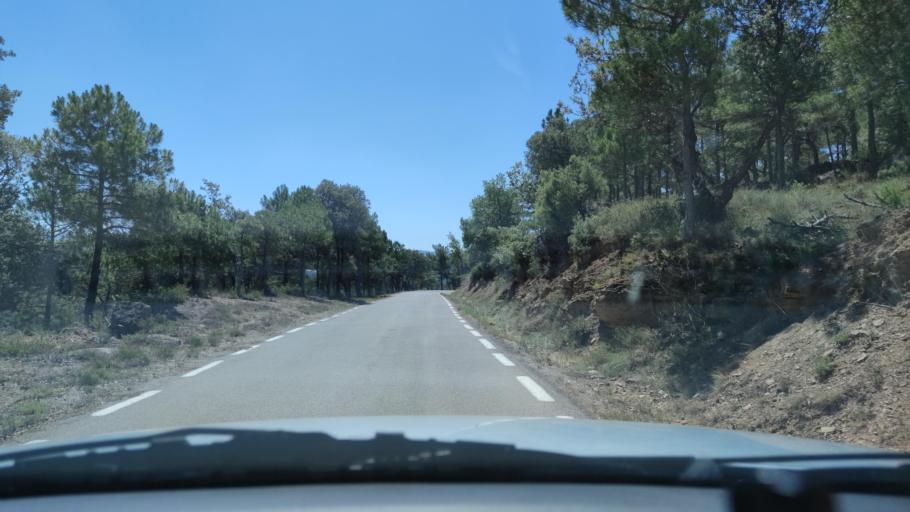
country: ES
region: Catalonia
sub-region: Provincia de Lleida
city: Tora de Riubregos
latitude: 41.8588
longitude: 1.4341
